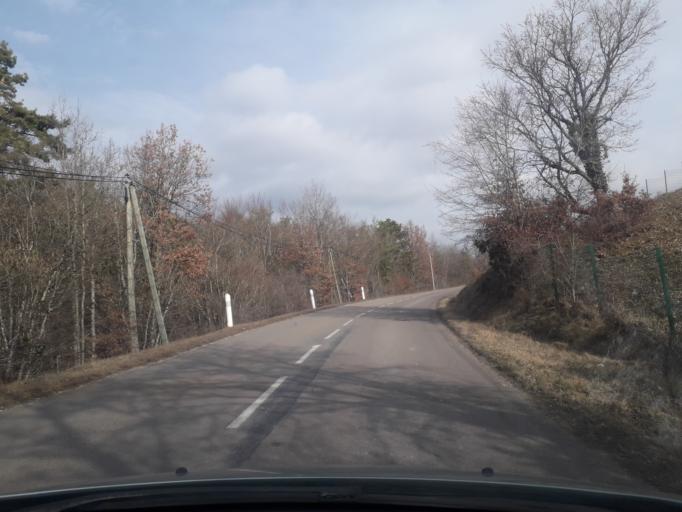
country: FR
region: Bourgogne
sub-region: Departement de la Cote-d'Or
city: Messigny-et-Vantoux
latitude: 47.4107
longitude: 5.0074
